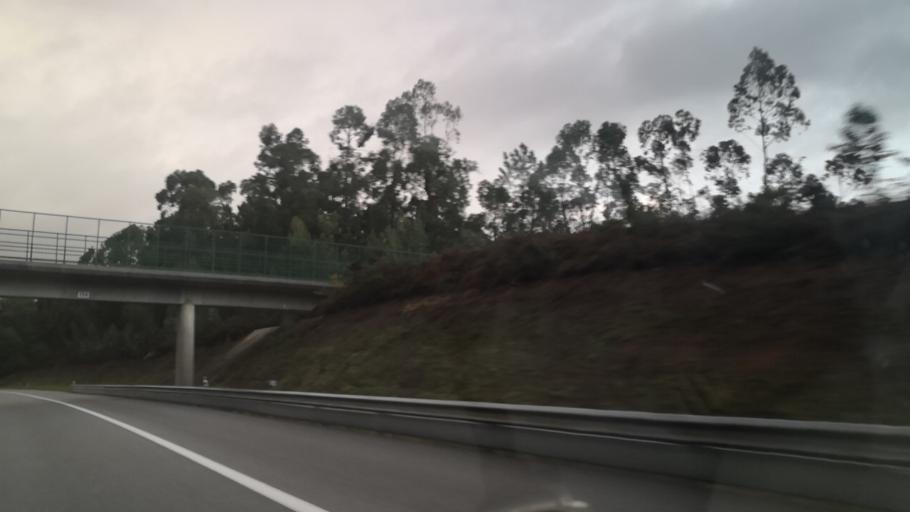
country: PT
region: Viana do Castelo
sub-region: Ponte de Lima
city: Ponte de Lima
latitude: 41.7493
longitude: -8.5566
